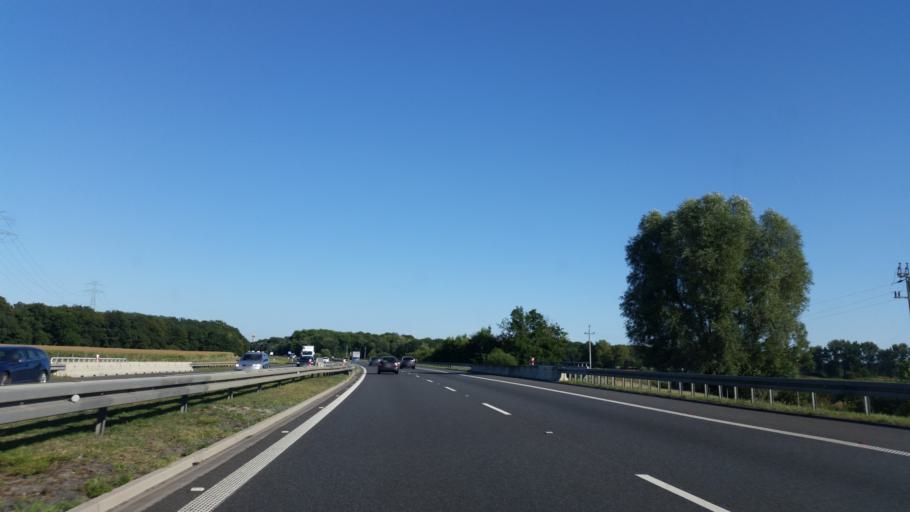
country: PL
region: Lower Silesian Voivodeship
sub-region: Powiat strzelinski
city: Wiazow
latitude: 50.8518
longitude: 17.2338
